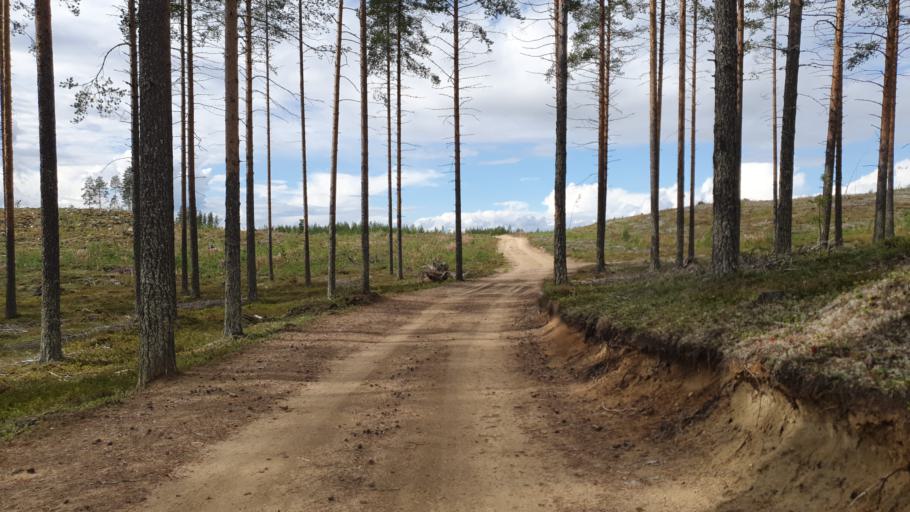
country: FI
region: Kainuu
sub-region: Kehys-Kainuu
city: Kuhmo
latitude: 64.1485
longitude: 29.3747
